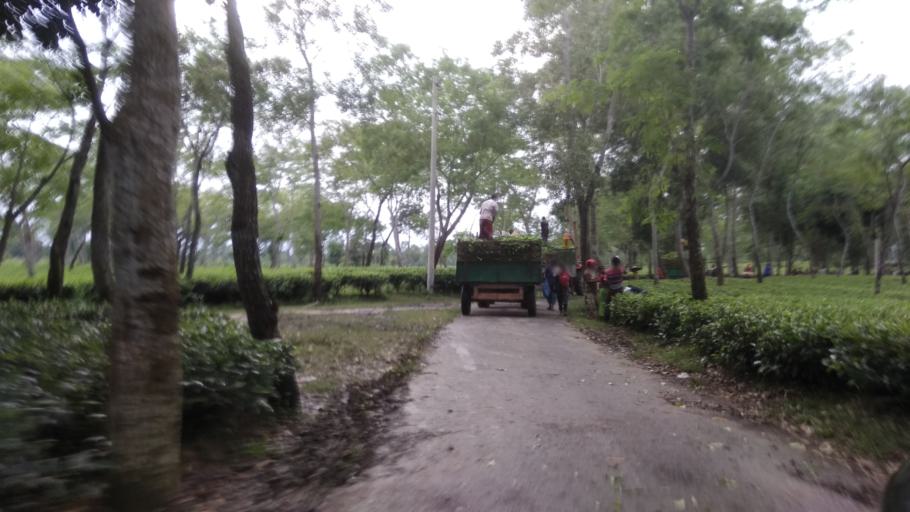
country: IN
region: Tripura
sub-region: Dhalai
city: Kamalpur
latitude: 24.1773
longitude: 91.8750
